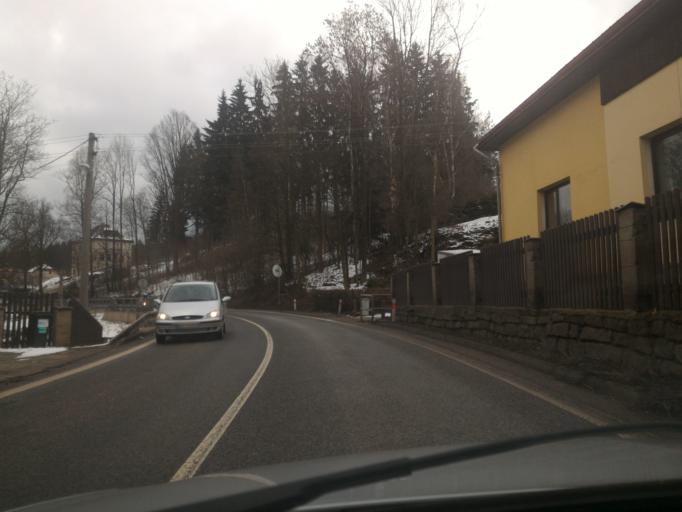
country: CZ
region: Liberecky
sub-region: Okres Jablonec nad Nisou
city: Lucany nad Nisou
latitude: 50.7389
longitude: 15.2093
